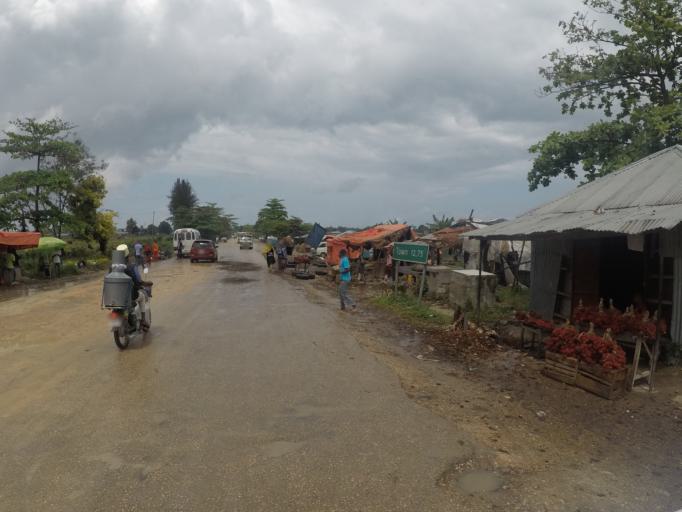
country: TZ
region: Zanzibar Central/South
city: Koani
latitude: -6.0747
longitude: 39.2236
